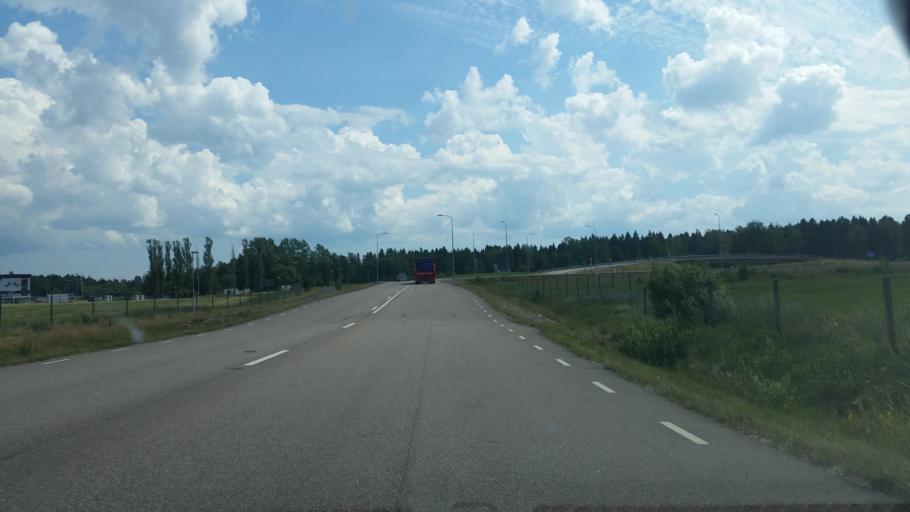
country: SE
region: Vaestra Goetaland
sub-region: Skara Kommun
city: Axvall
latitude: 58.3988
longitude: 13.5591
